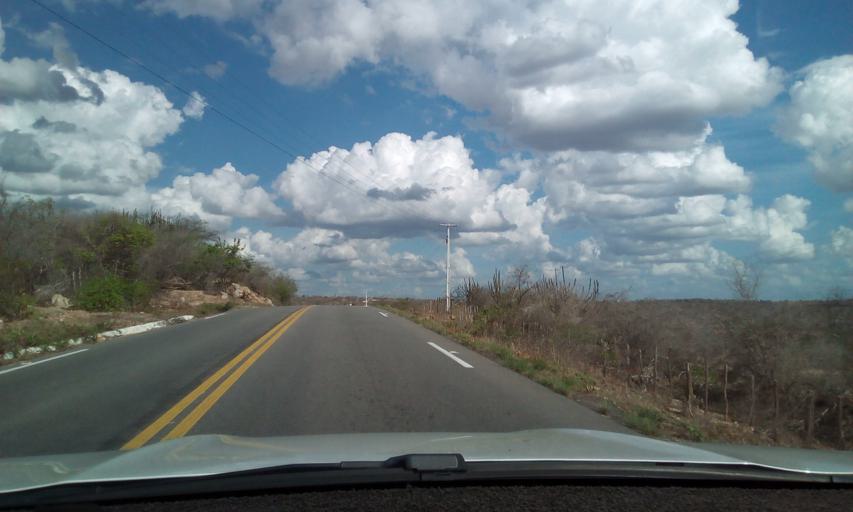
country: BR
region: Rio Grande do Norte
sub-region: Parelhas
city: Parelhas
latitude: -6.7945
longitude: -36.4179
